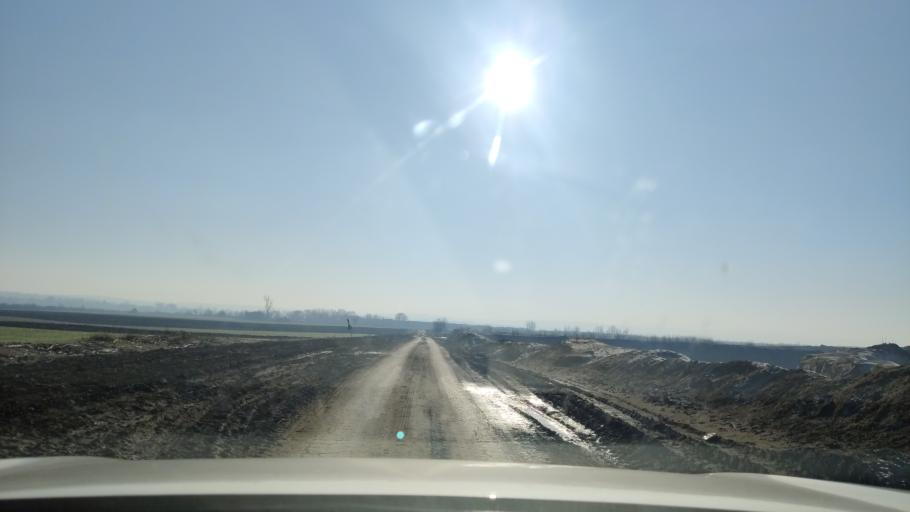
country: RS
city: Ostruznica
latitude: 44.7308
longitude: 20.2816
